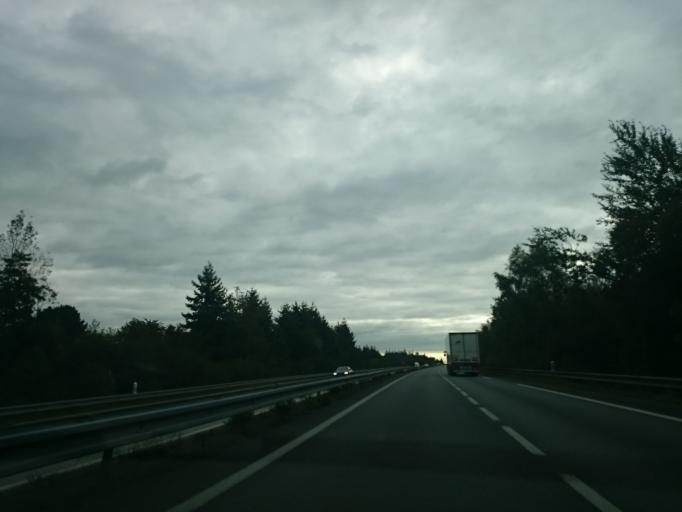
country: FR
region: Brittany
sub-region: Departement du Morbihan
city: Branderion
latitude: 47.7819
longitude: -3.2039
